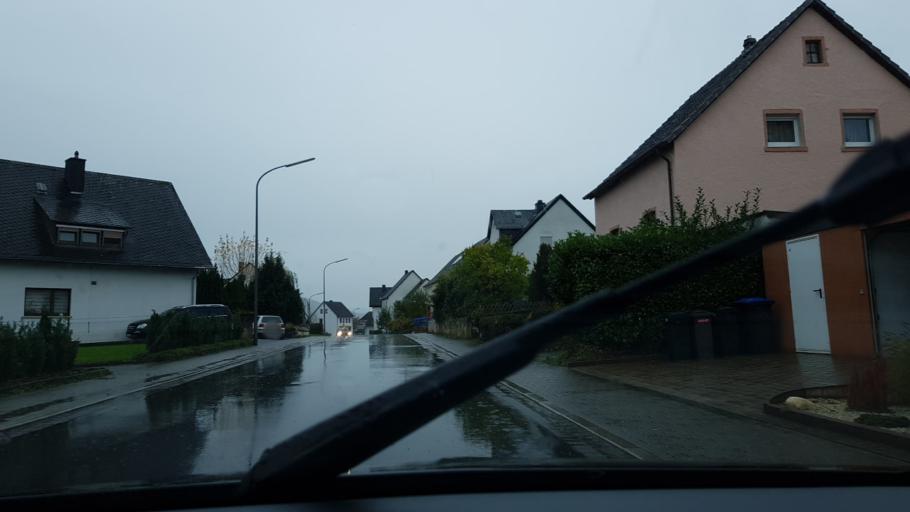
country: DE
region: Rheinland-Pfalz
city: Neuerburg
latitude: 49.9764
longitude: 6.9378
